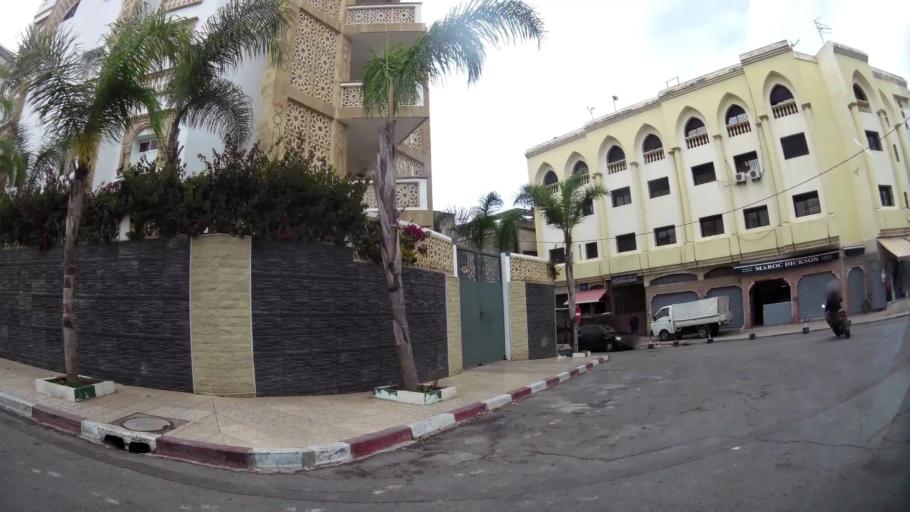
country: MA
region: Grand Casablanca
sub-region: Casablanca
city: Casablanca
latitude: 33.5837
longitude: -7.6062
